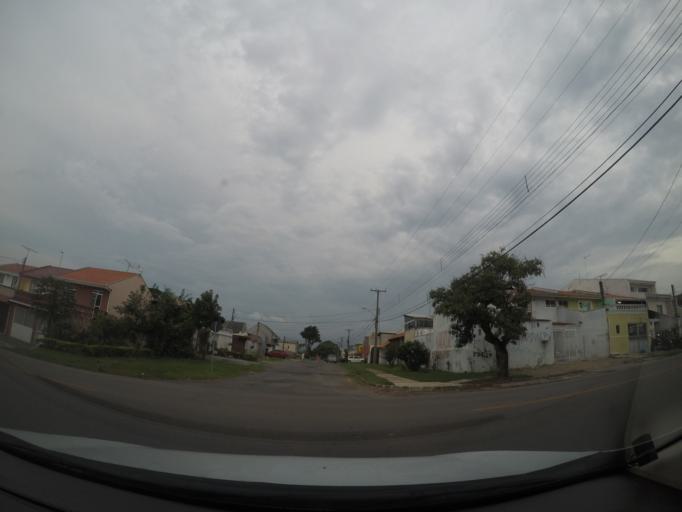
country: BR
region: Parana
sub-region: Sao Jose Dos Pinhais
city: Sao Jose dos Pinhais
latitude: -25.5159
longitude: -49.2360
